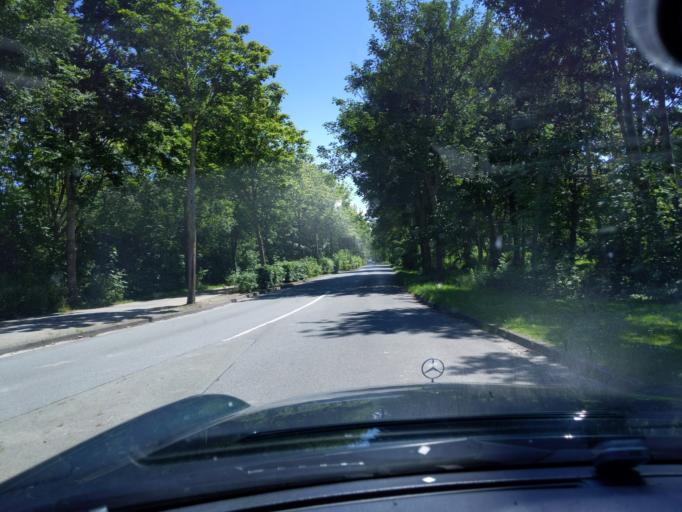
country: DE
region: Lower Saxony
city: Butjadingen
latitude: 53.5753
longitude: 8.2518
